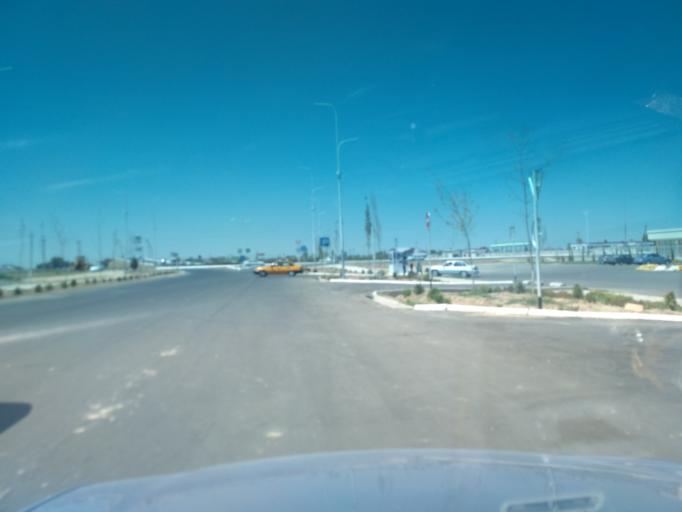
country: UZ
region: Sirdaryo
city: Guliston
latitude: 40.4752
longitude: 68.7781
